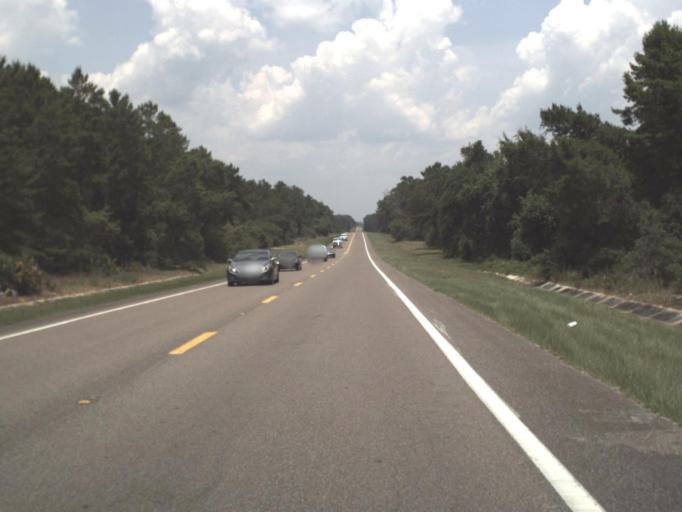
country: US
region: Florida
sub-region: Putnam County
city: Crescent City
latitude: 29.3736
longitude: -81.7358
